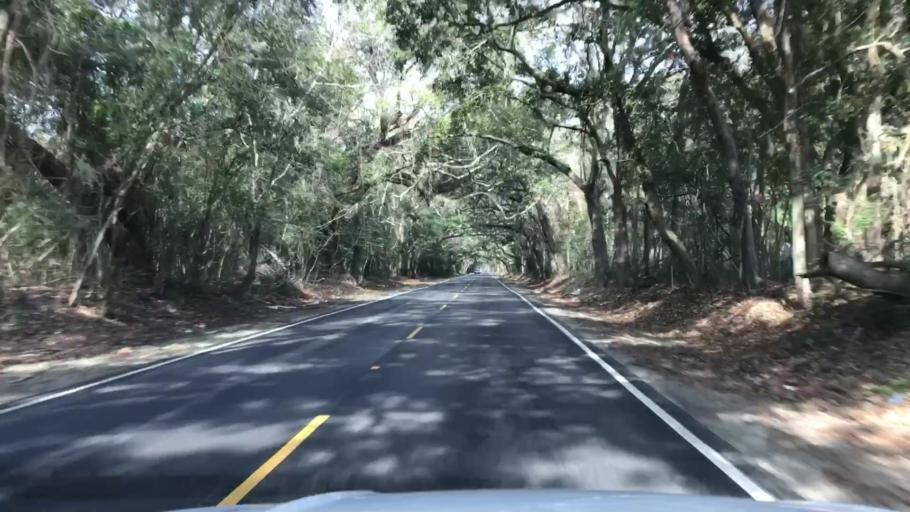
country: US
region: South Carolina
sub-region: Charleston County
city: Folly Beach
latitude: 32.7071
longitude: -80.0168
